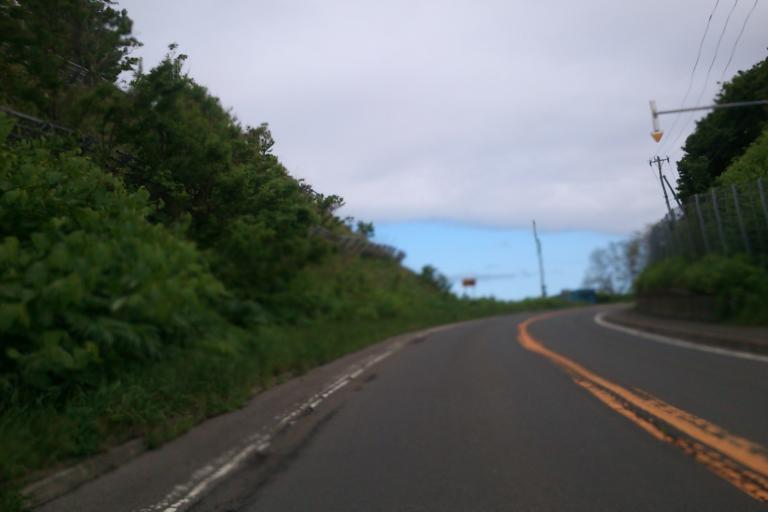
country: JP
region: Hokkaido
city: Ishikari
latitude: 43.4141
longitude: 141.4320
